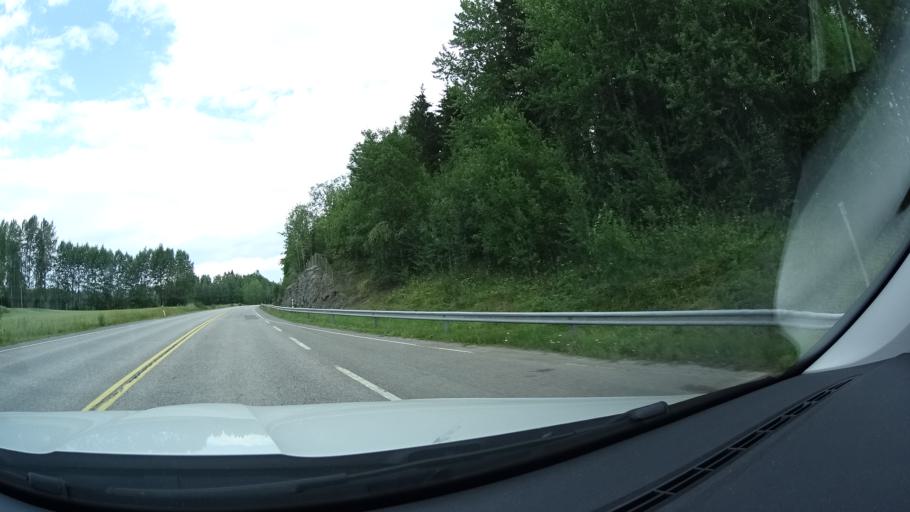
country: FI
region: Uusimaa
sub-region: Helsinki
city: Espoo
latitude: 60.1685
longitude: 24.5487
